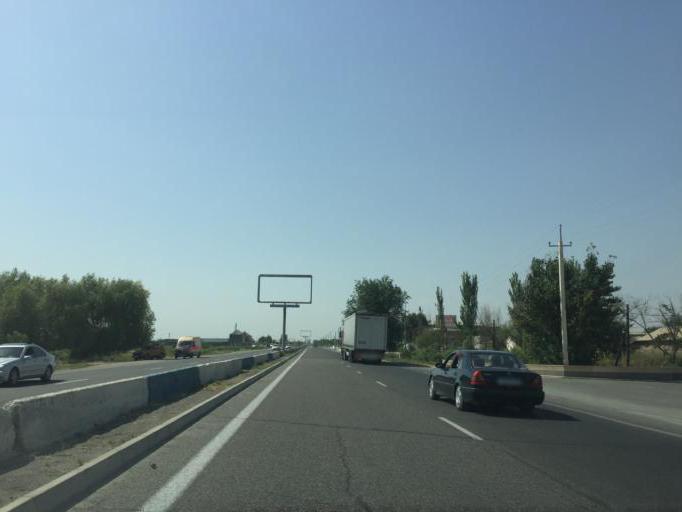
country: AM
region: Ararat
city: Shahumyan
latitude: 39.9423
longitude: 44.5539
